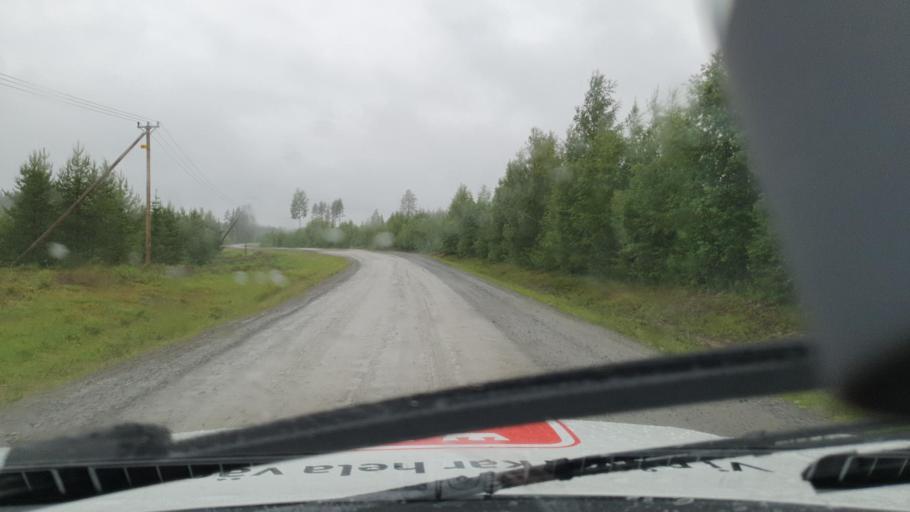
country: SE
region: Vaesterbotten
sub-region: Bjurholms Kommun
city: Bjurholm
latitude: 63.9245
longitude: 19.3710
